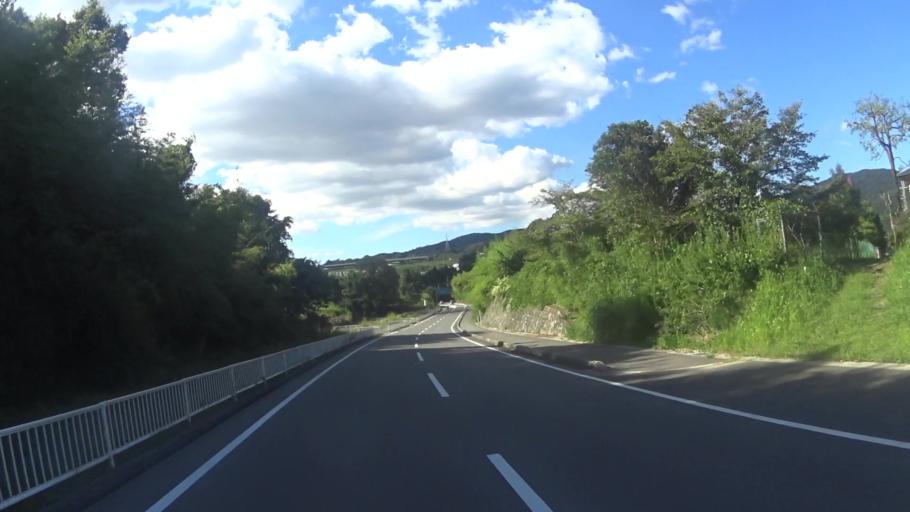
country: JP
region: Kyoto
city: Uji
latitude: 34.8424
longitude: 135.8437
